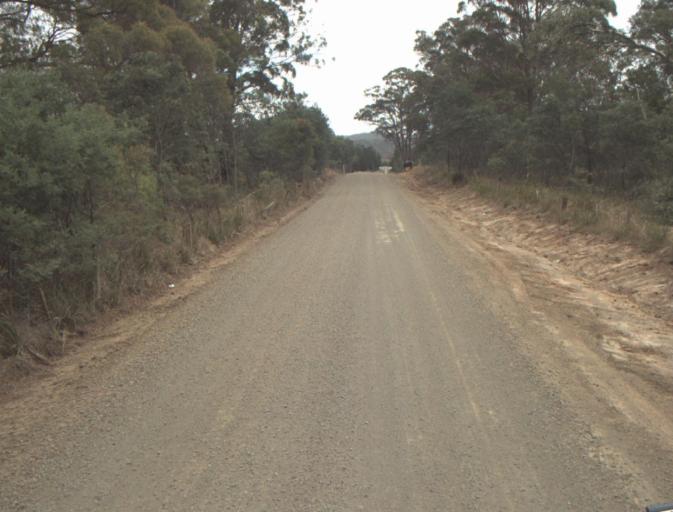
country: AU
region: Tasmania
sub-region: Northern Midlands
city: Evandale
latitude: -41.5124
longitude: 147.3476
